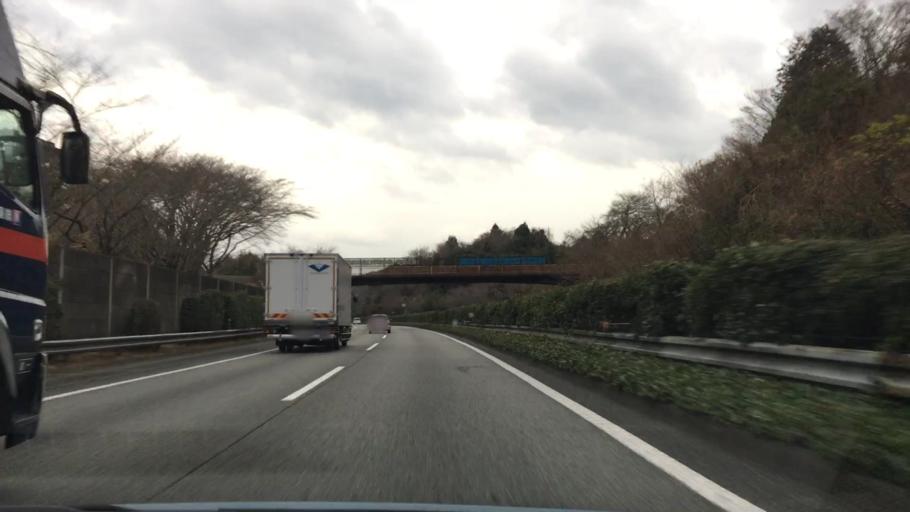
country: JP
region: Shizuoka
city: Fujinomiya
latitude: 35.1459
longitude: 138.6140
